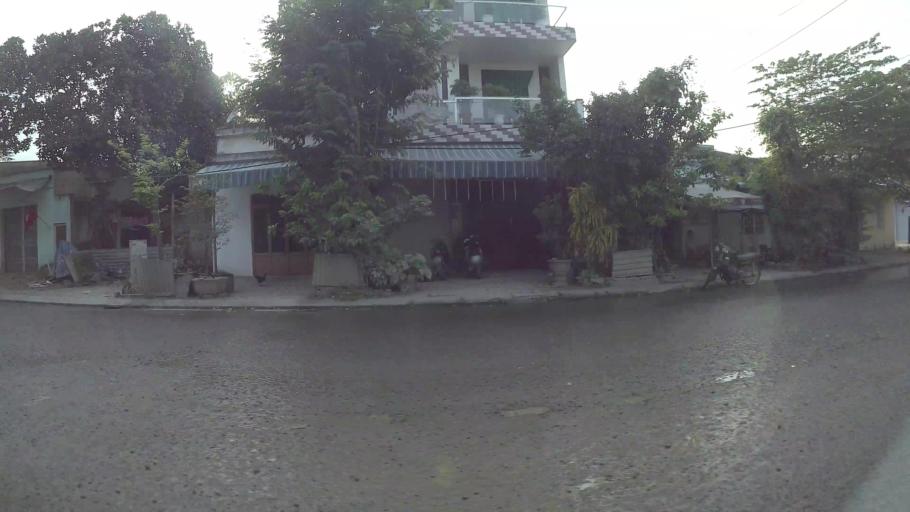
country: VN
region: Da Nang
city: Lien Chieu
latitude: 16.0501
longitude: 108.1513
